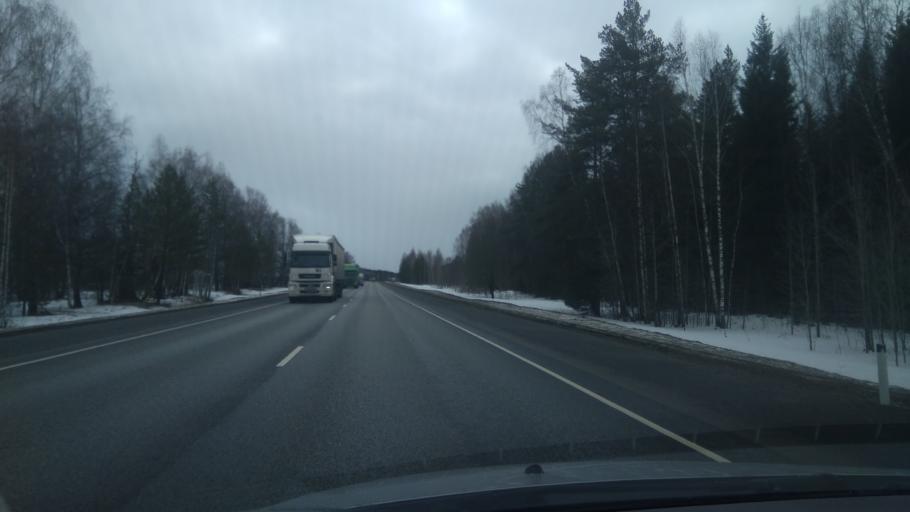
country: RU
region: Perm
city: Suksun
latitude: 56.9151
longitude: 57.5803
